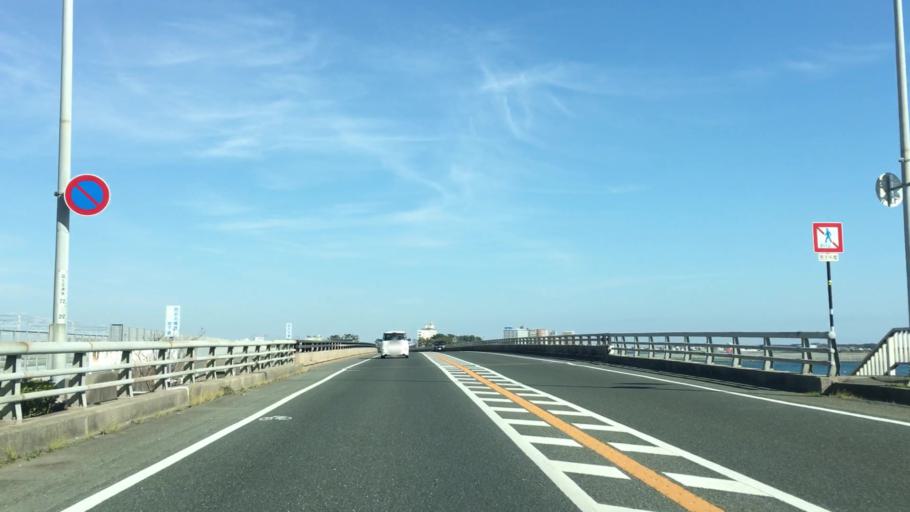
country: JP
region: Shizuoka
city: Kosai-shi
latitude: 34.6939
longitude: 137.5842
